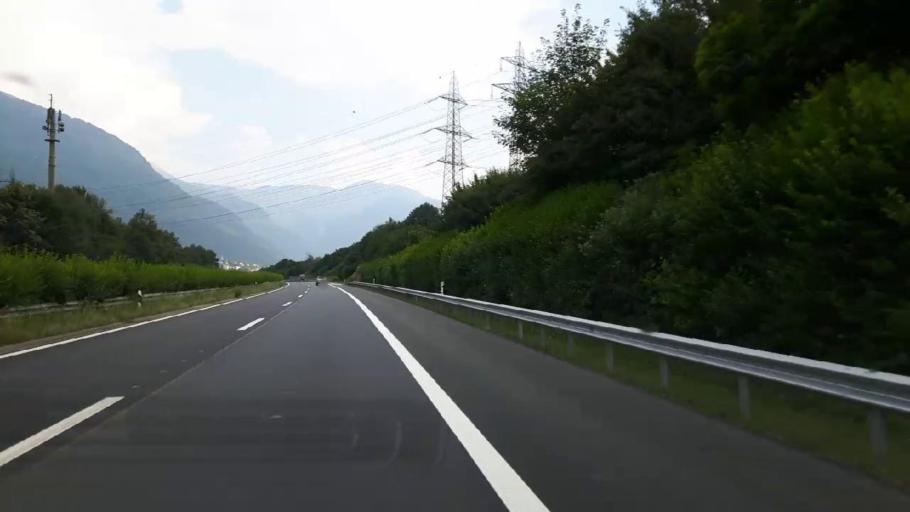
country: CH
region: Ticino
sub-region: Riviera District
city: Claro
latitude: 46.2735
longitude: 8.9984
